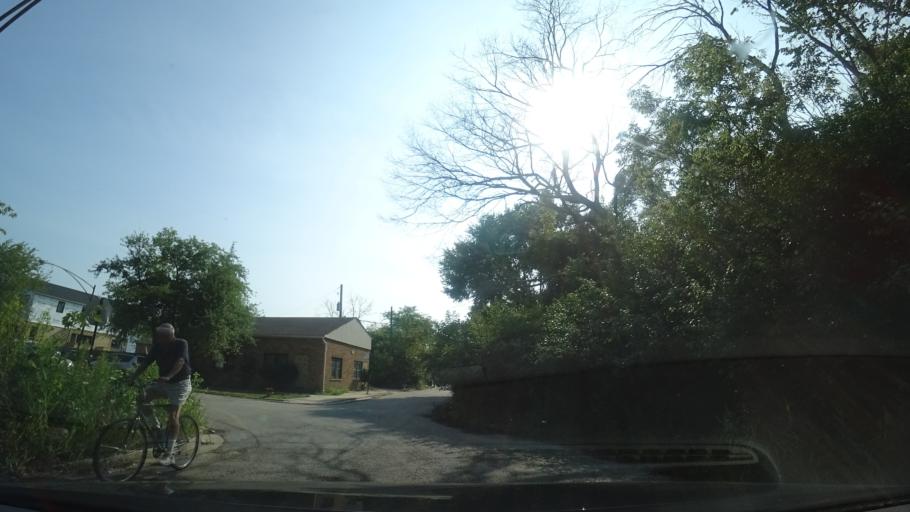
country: US
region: Illinois
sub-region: Cook County
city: Lincolnwood
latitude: 41.9827
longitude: -87.7386
